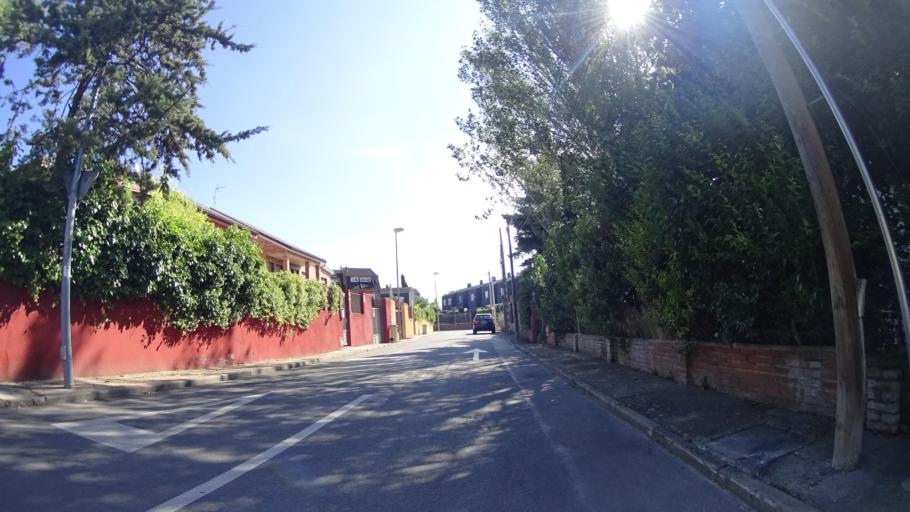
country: ES
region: Madrid
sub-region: Provincia de Madrid
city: Las Matas
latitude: 40.5465
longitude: -3.8917
